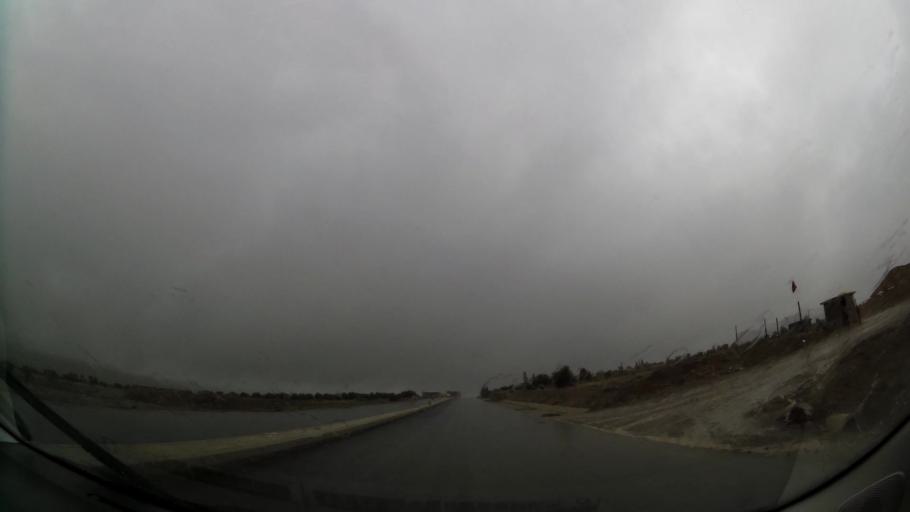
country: MA
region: Oriental
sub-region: Nador
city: Midar
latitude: 34.8630
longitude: -3.7236
